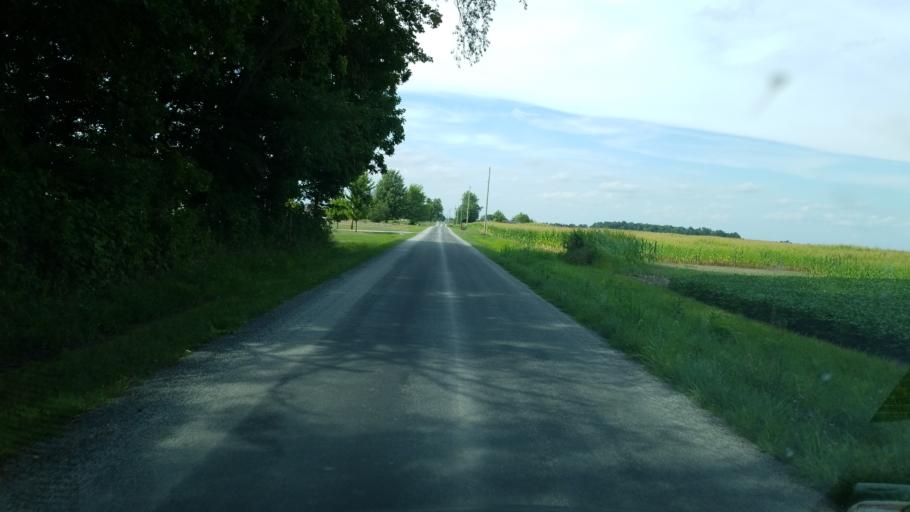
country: US
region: Ohio
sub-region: Delaware County
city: Ashley
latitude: 40.4624
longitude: -82.9888
